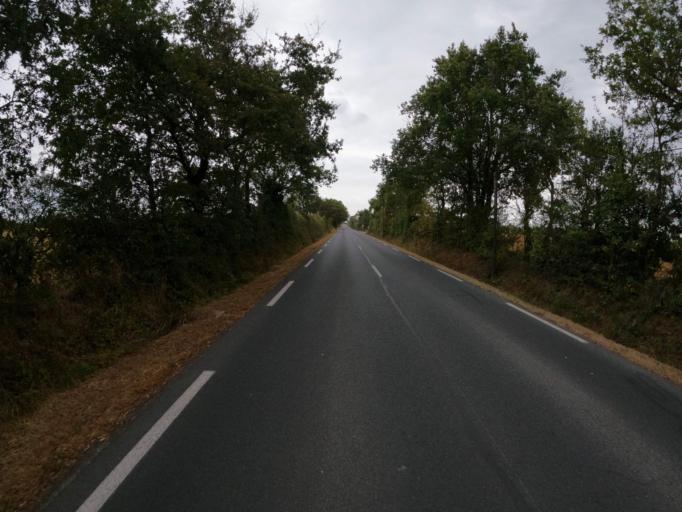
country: FR
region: Pays de la Loire
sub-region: Departement de la Vendee
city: La Bruffiere
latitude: 46.9962
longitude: -1.1592
